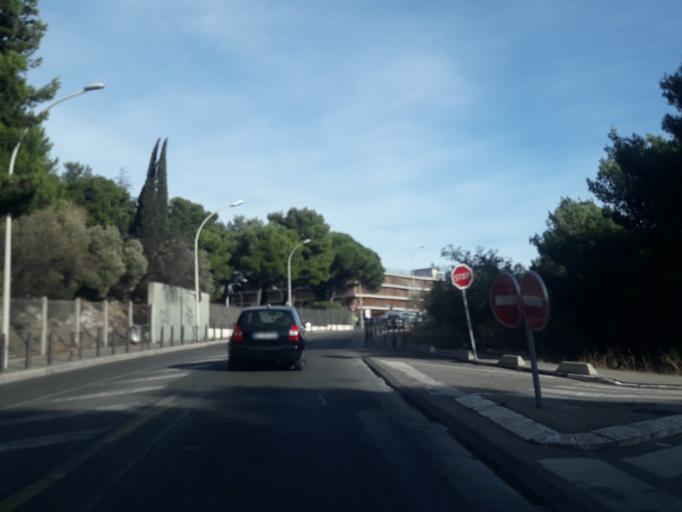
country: FR
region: Provence-Alpes-Cote d'Azur
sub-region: Departement des Bouches-du-Rhone
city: Marseille 15
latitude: 43.3775
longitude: 5.3613
